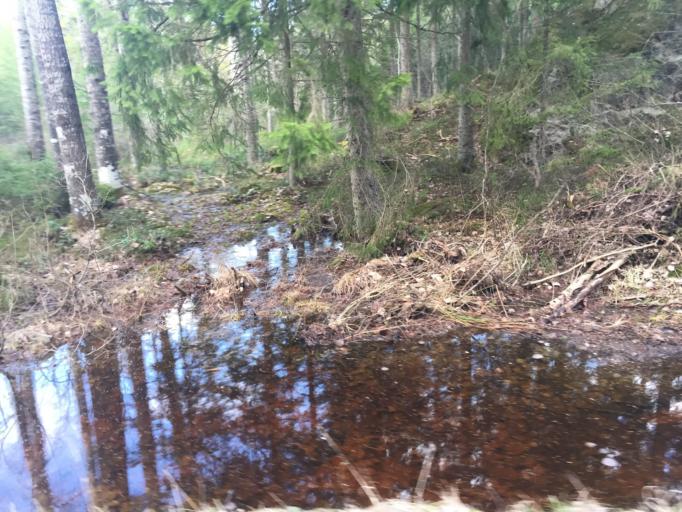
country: SE
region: Soedermanland
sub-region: Vingakers Kommun
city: Vingaker
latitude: 58.9932
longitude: 15.6824
